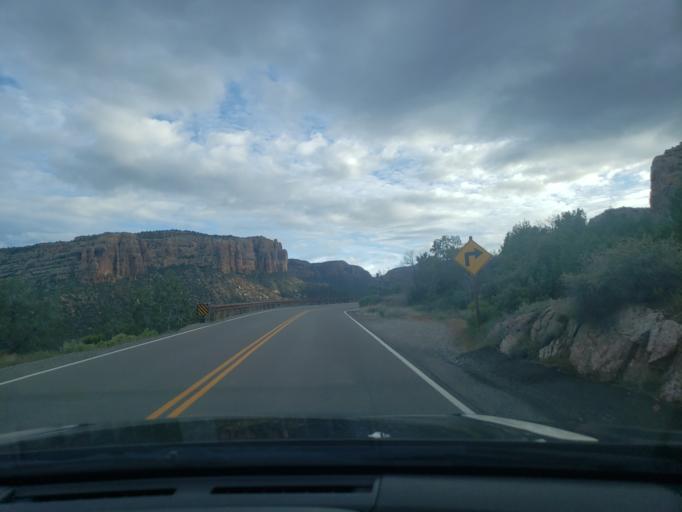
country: US
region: Colorado
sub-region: Mesa County
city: Redlands
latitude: 39.0264
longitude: -108.6406
